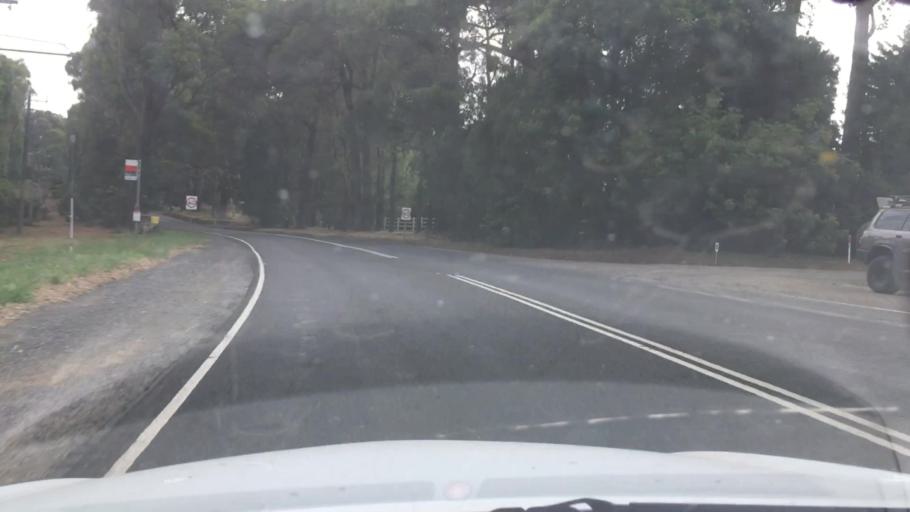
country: AU
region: Victoria
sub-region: Cardinia
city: Emerald
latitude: -37.9330
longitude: 145.4196
